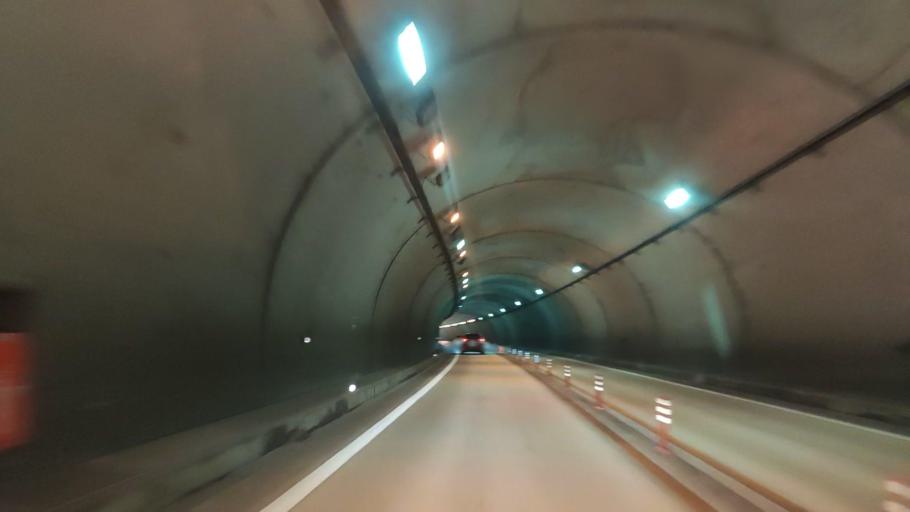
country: JP
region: Hiroshima
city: Innoshima
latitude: 34.2936
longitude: 133.1436
